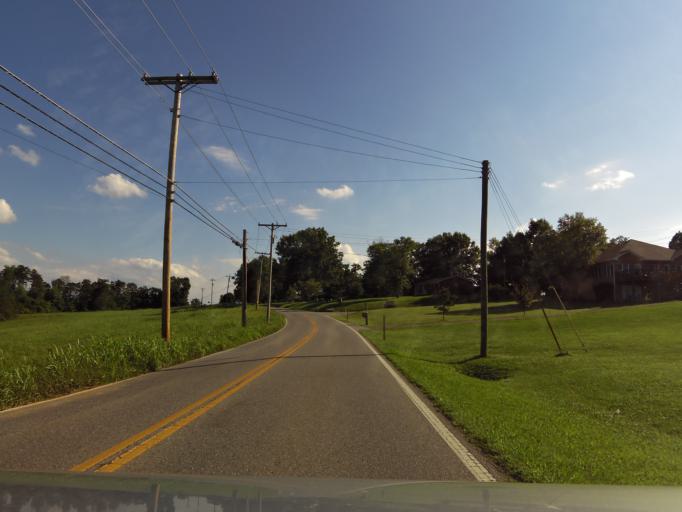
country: US
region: Tennessee
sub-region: Blount County
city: Louisville
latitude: 35.7637
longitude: -84.0327
